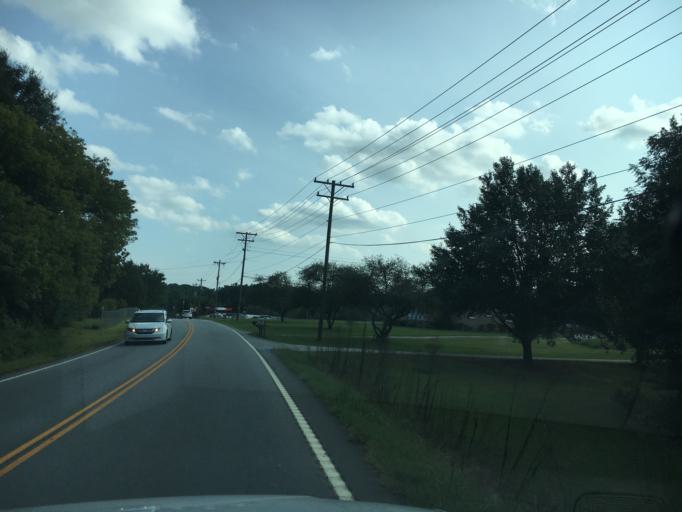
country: US
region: South Carolina
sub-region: Greenville County
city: Taylors
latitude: 34.9804
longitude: -82.2793
